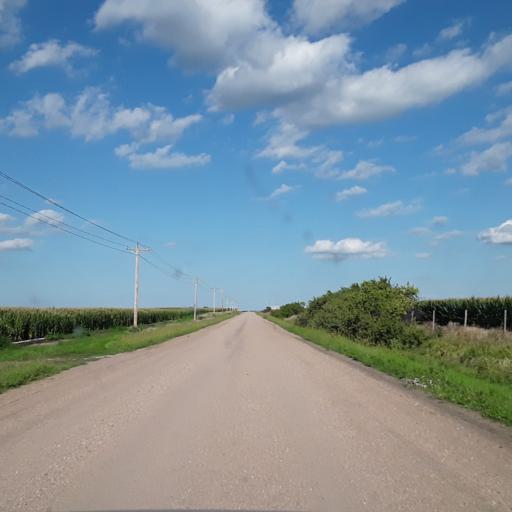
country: US
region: Nebraska
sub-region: Hall County
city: Wood River
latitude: 40.9169
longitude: -98.6051
